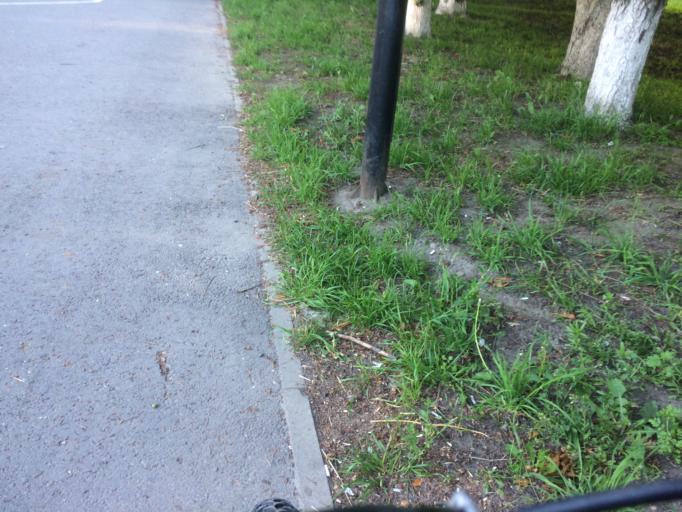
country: RU
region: Kursk
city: Kursk
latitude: 51.6686
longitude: 36.1418
